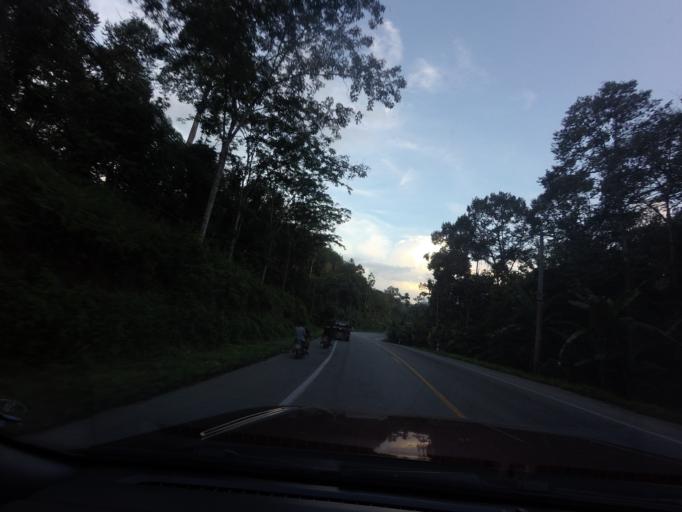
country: TH
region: Yala
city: Than To
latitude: 6.0960
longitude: 101.1798
